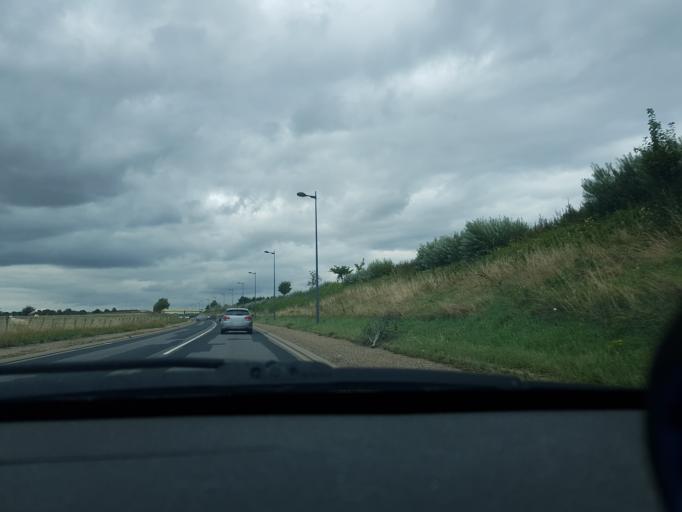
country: FR
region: Lorraine
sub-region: Departement de Meurthe-et-Moselle
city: Saulxures-les-Nancy
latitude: 48.6899
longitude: 6.2372
